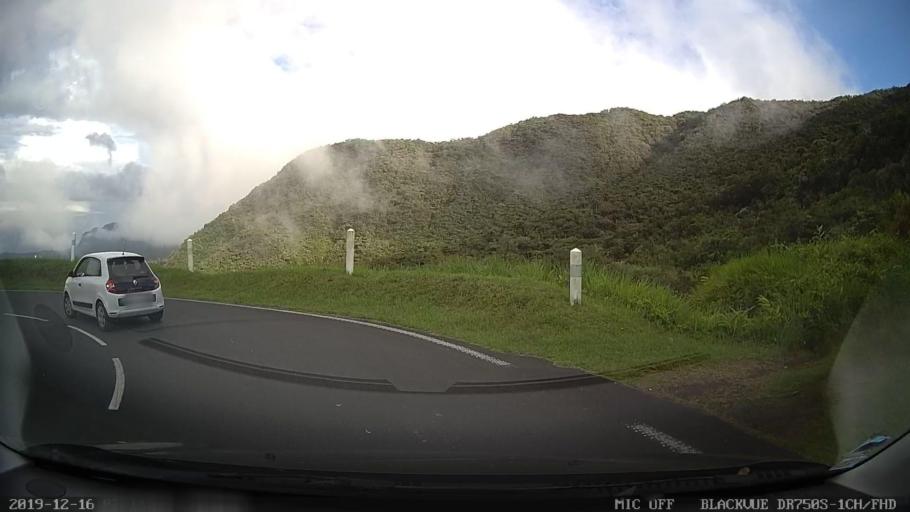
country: RE
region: Reunion
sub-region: Reunion
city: Cilaos
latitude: -21.1591
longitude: 55.5970
